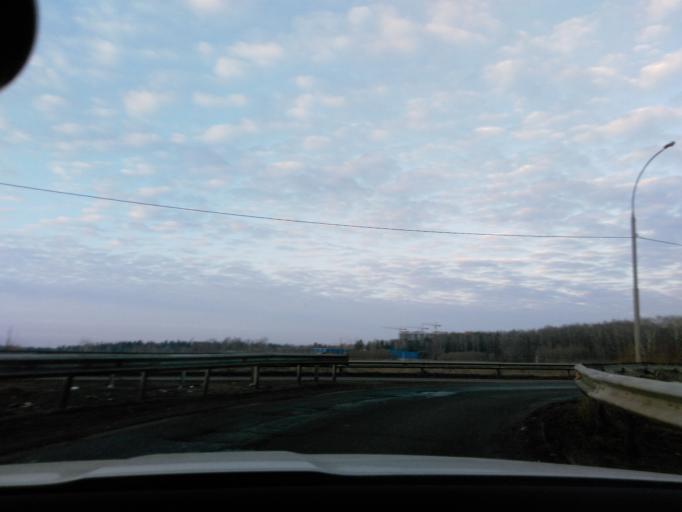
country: RU
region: Moskovskaya
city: Novopodrezkovo
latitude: 55.9646
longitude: 37.3290
